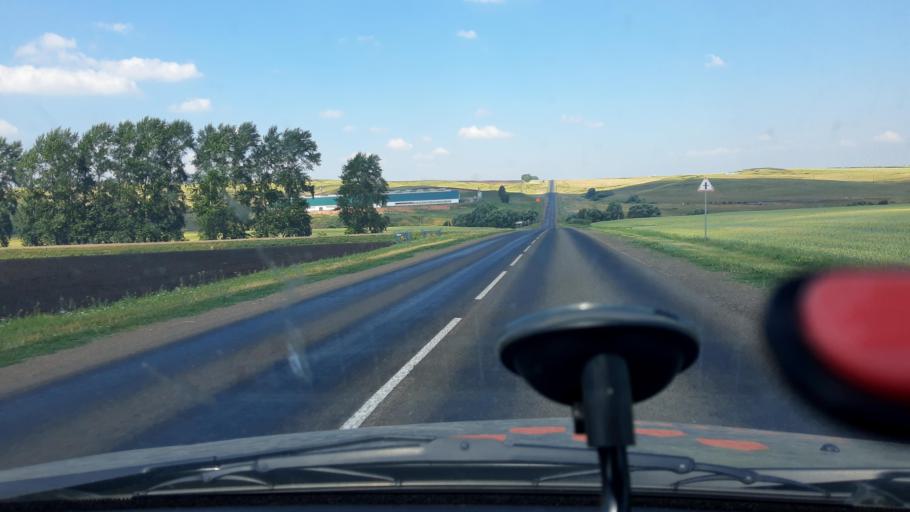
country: RU
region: Bashkortostan
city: Chekmagush
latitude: 55.0580
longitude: 54.6246
